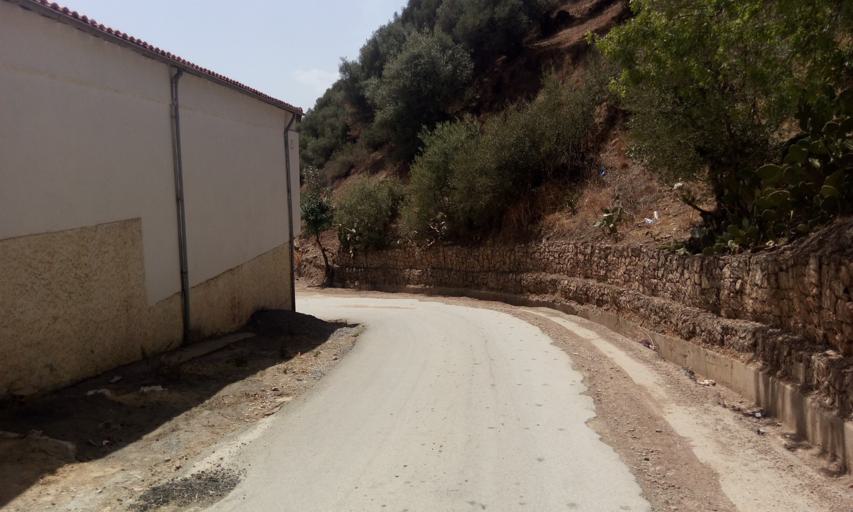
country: DZ
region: Tizi Ouzou
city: Chemini
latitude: 36.6073
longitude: 4.6316
